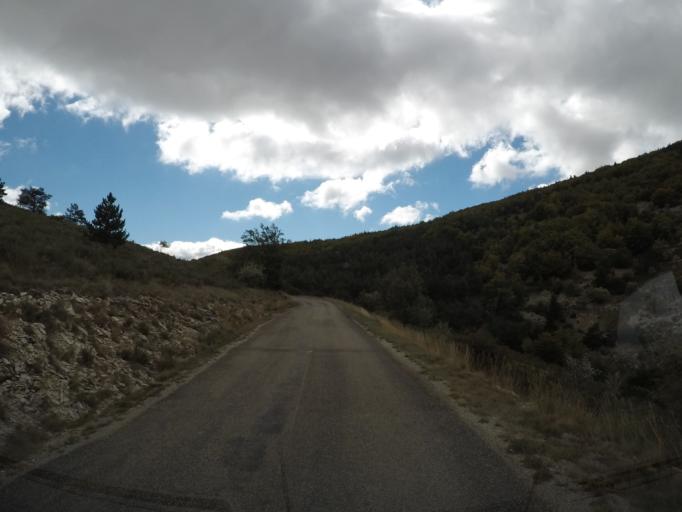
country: FR
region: Provence-Alpes-Cote d'Azur
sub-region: Departement du Vaucluse
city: Sault
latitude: 44.1660
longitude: 5.4963
